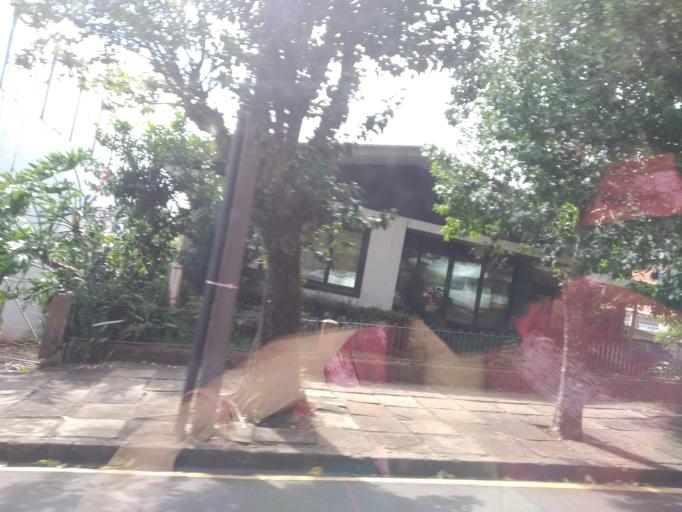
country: BR
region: Parana
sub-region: Pato Branco
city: Pato Branco
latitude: -26.2303
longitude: -52.6702
